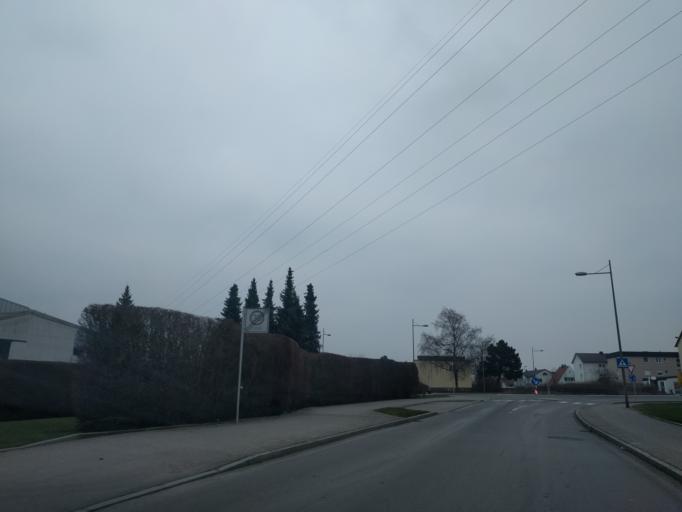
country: DE
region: Bavaria
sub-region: Swabia
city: Donauwoerth
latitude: 48.7158
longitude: 10.7476
